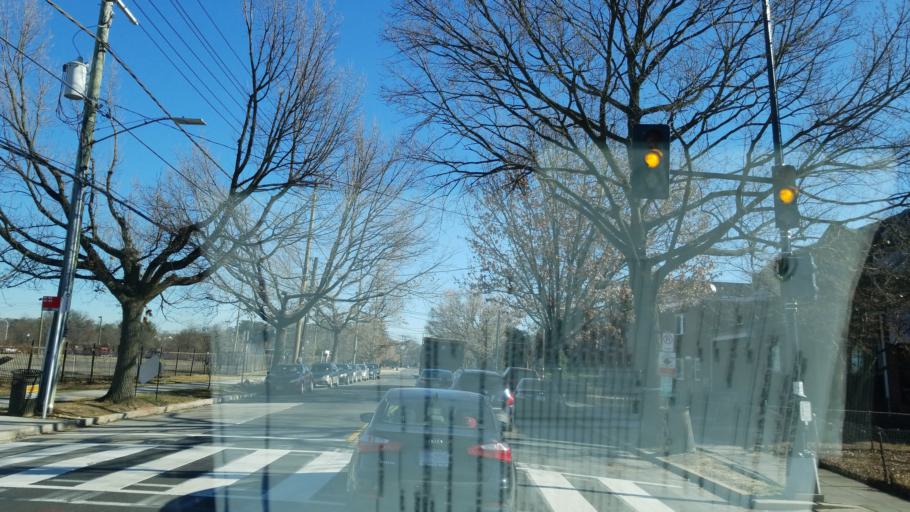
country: US
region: Maryland
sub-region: Prince George's County
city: Glassmanor
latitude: 38.8443
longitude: -76.9906
